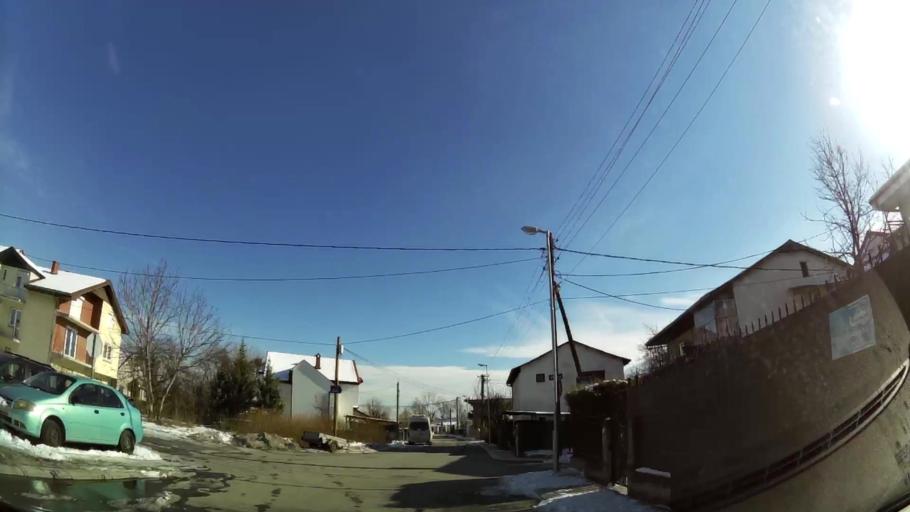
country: MK
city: Krushopek
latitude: 42.0023
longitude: 21.3554
